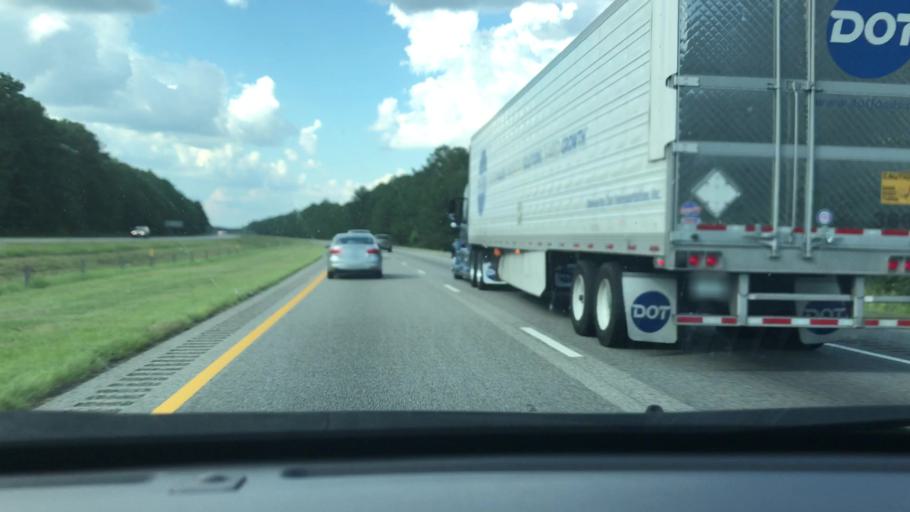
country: US
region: South Carolina
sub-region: Florence County
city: Timmonsville
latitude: 34.0093
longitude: -79.9991
